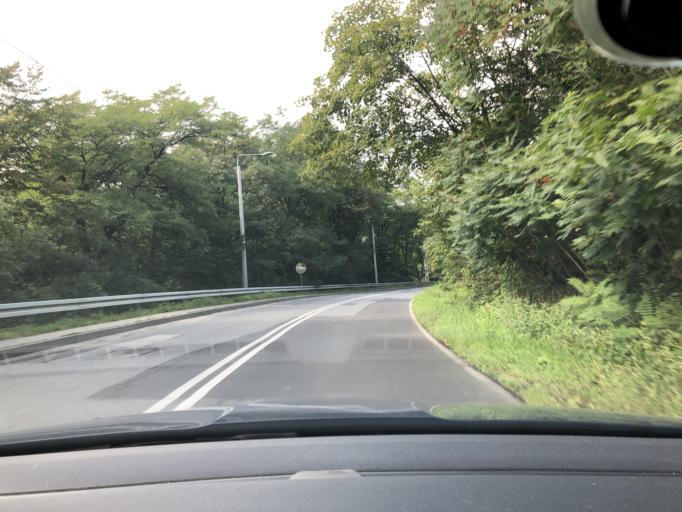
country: PL
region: Silesian Voivodeship
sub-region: Powiat zywiecki
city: Czernichow
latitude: 49.7432
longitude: 19.2114
